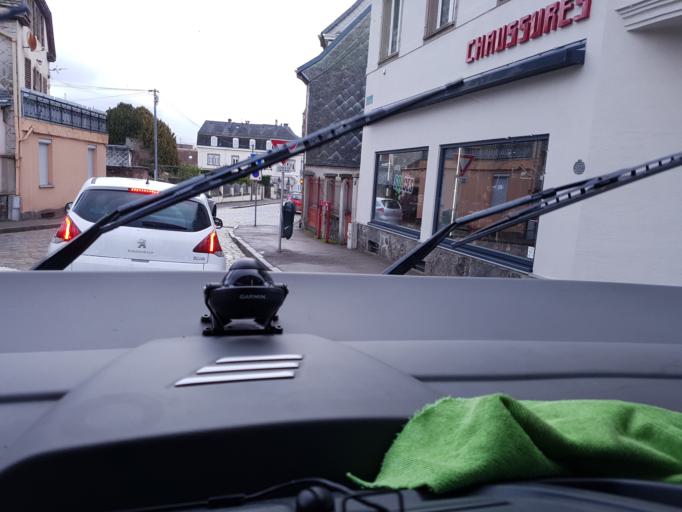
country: FR
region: Alsace
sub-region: Departement du Haut-Rhin
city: Munster
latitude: 48.0411
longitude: 7.1325
